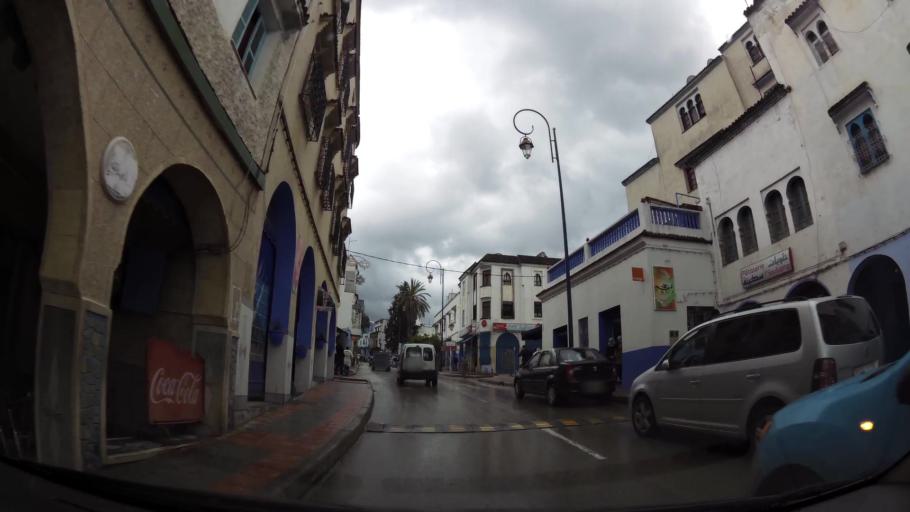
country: MA
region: Tanger-Tetouan
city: Chefchaouene
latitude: 35.1694
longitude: -5.2703
